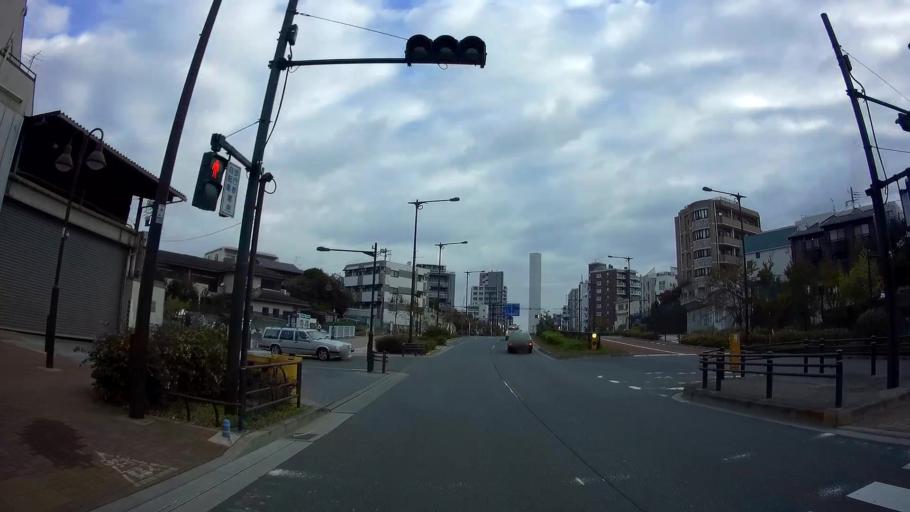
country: JP
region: Tokyo
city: Tokyo
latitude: 35.7176
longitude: 139.6880
